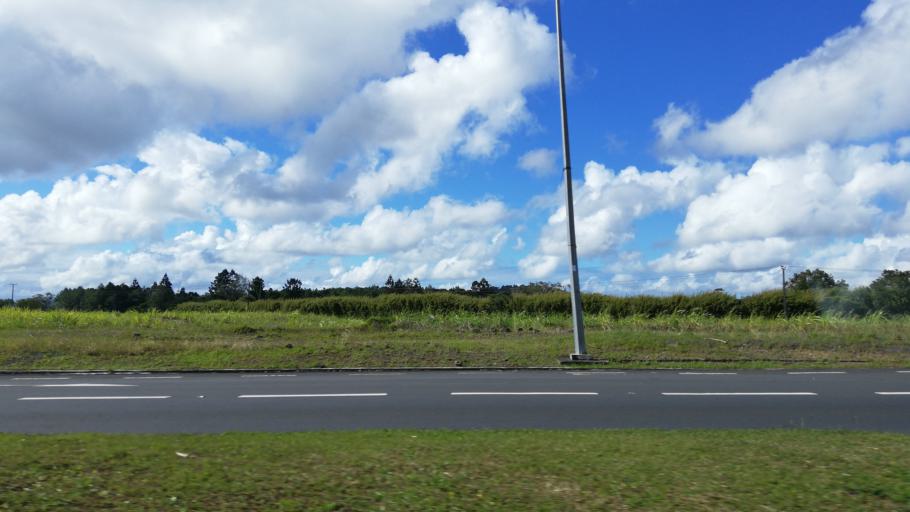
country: MU
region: Moka
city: Quartier Militaire
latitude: -20.2542
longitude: 57.5838
